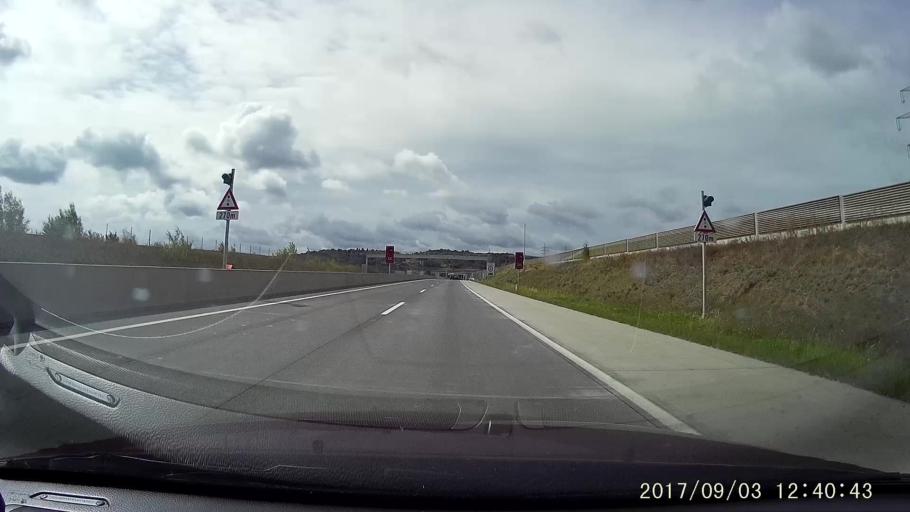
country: AT
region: Lower Austria
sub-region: Politischer Bezirk Korneuburg
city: Enzersfeld
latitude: 48.3440
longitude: 16.4302
